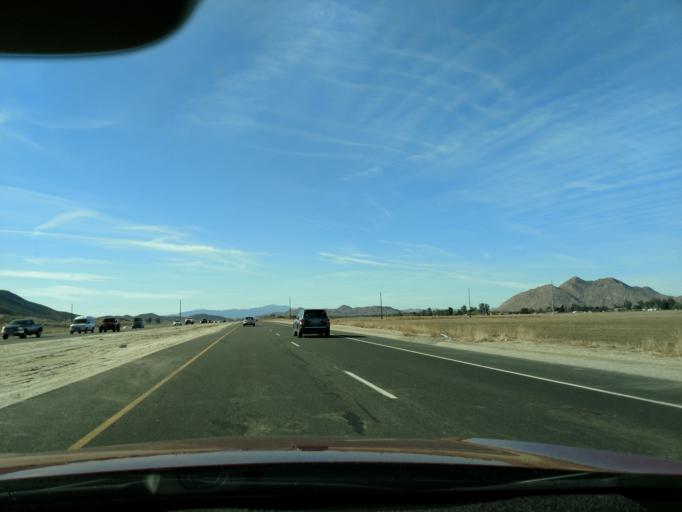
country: US
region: California
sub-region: Riverside County
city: Winchester
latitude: 33.6963
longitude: -117.0719
